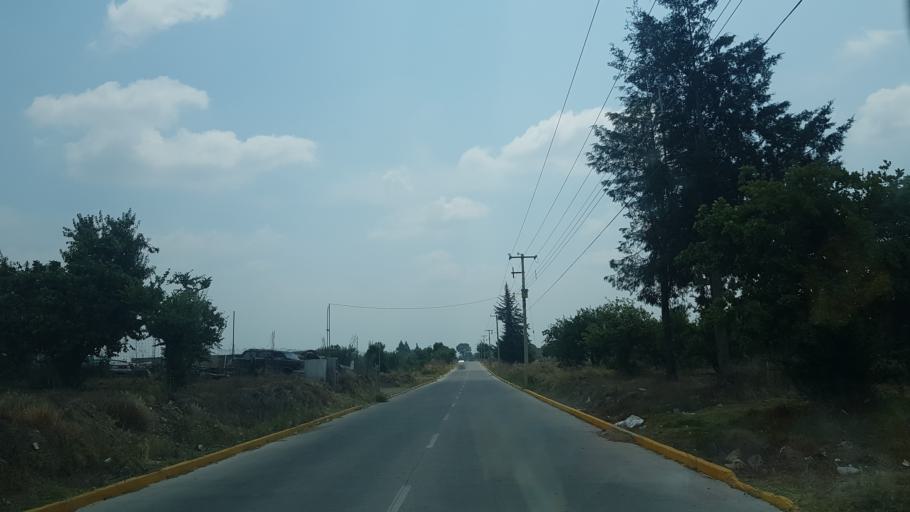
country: MX
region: Puebla
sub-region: Huejotzingo
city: San Juan Pancoac
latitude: 19.1384
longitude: -98.4346
